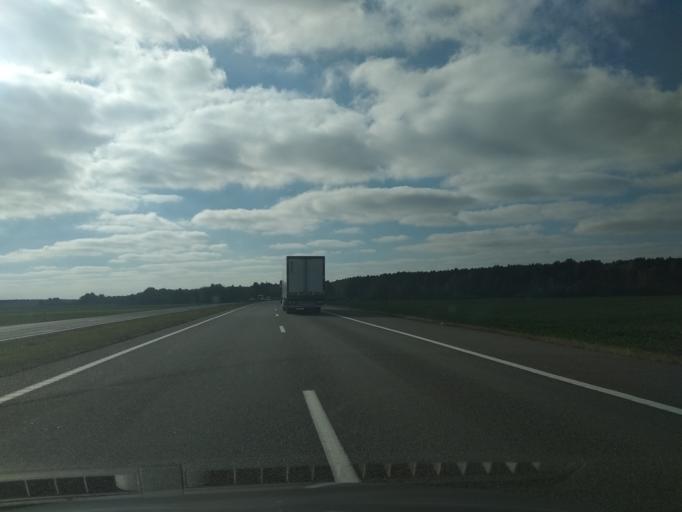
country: BY
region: Grodnenskaya
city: Mir
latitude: 53.4216
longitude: 26.5772
